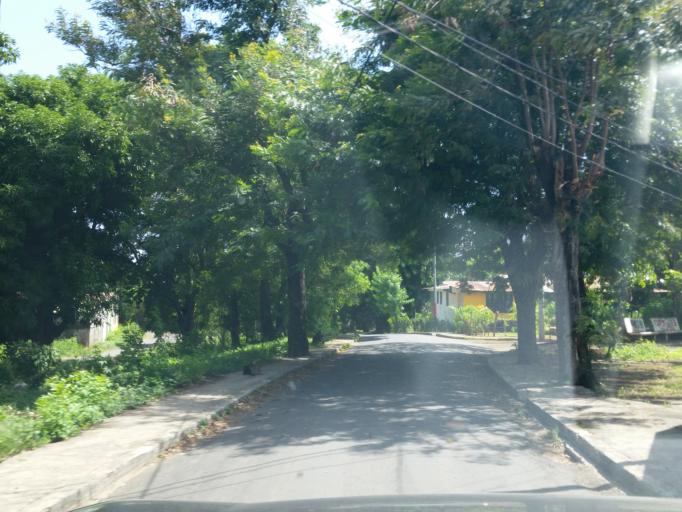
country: NI
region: Managua
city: Managua
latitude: 12.1106
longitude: -86.2505
